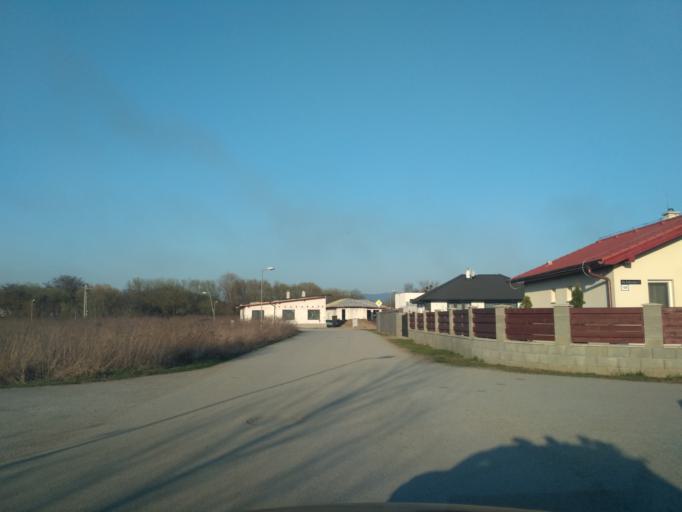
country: SK
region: Kosicky
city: Kosice
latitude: 48.6689
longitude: 21.3086
